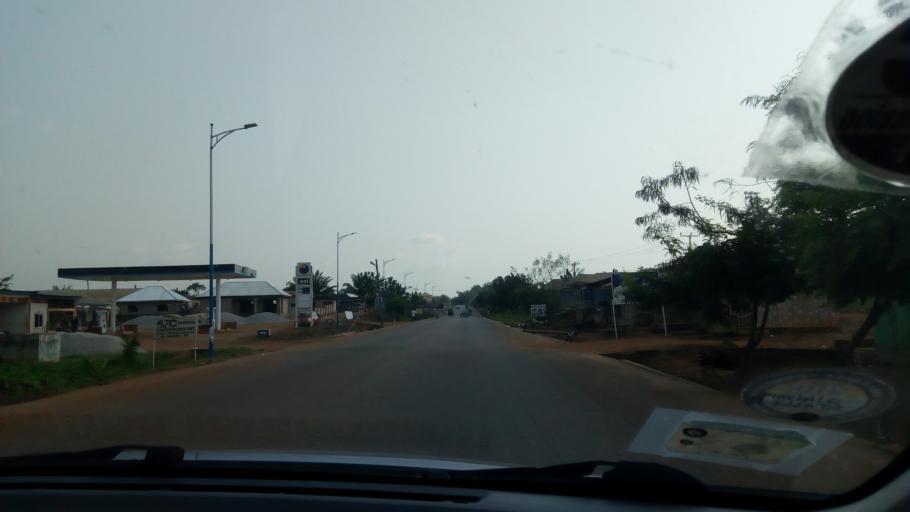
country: GH
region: Western
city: Bibiani
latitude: 6.7922
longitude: -2.5167
